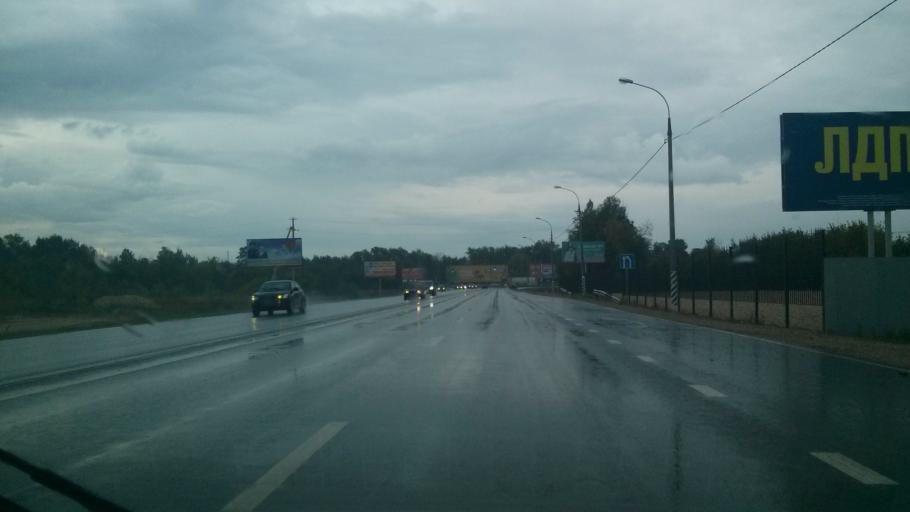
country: RU
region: Nizjnij Novgorod
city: Afonino
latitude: 56.2285
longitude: 44.0964
